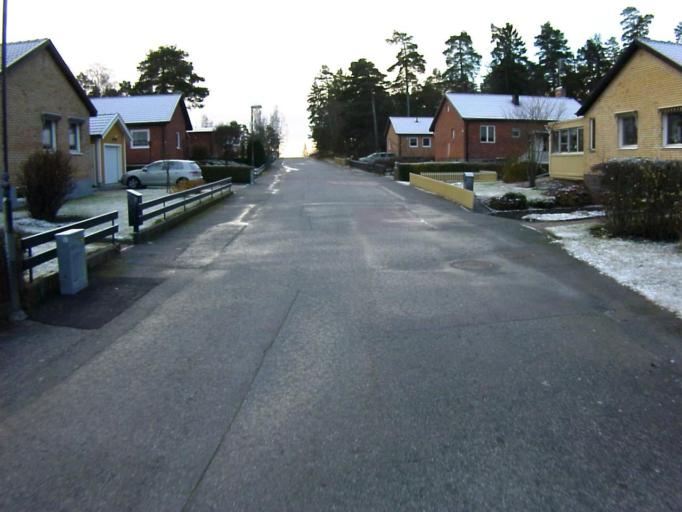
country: SE
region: Soedermanland
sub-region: Eskilstuna Kommun
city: Hallbybrunn
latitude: 59.3961
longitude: 16.4118
